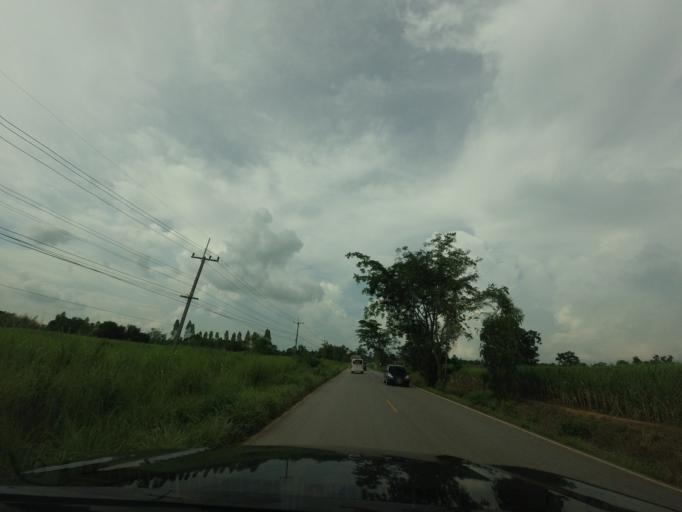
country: TH
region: Changwat Nong Bua Lamphu
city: Suwannakhuha
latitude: 17.4267
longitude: 102.3373
